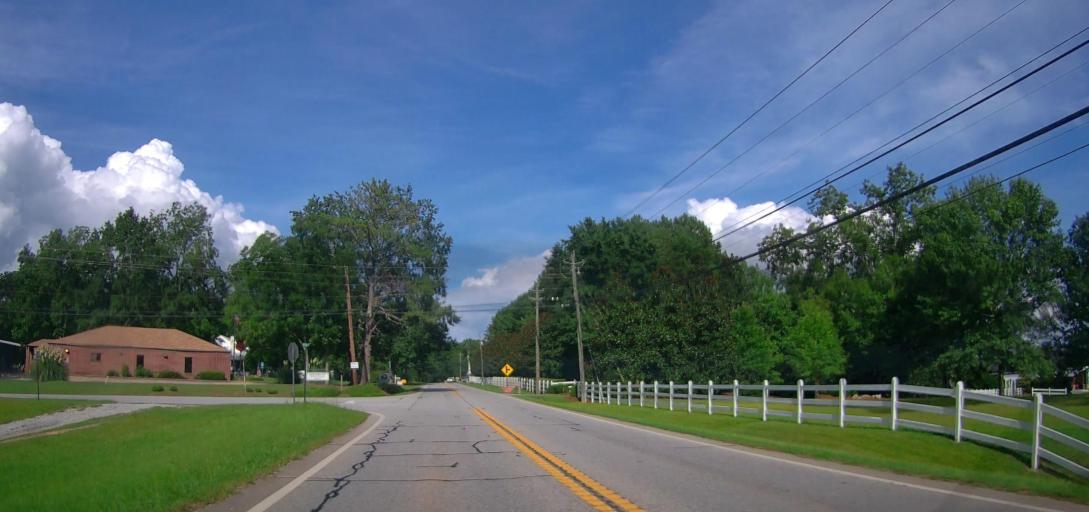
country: US
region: Georgia
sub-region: Harris County
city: Hamilton
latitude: 32.6403
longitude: -84.8863
